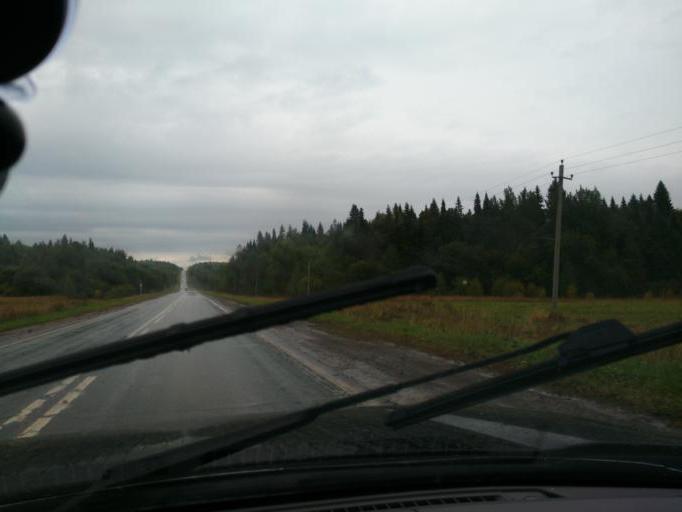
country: RU
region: Perm
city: Kultayevo
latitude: 57.8260
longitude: 55.8089
